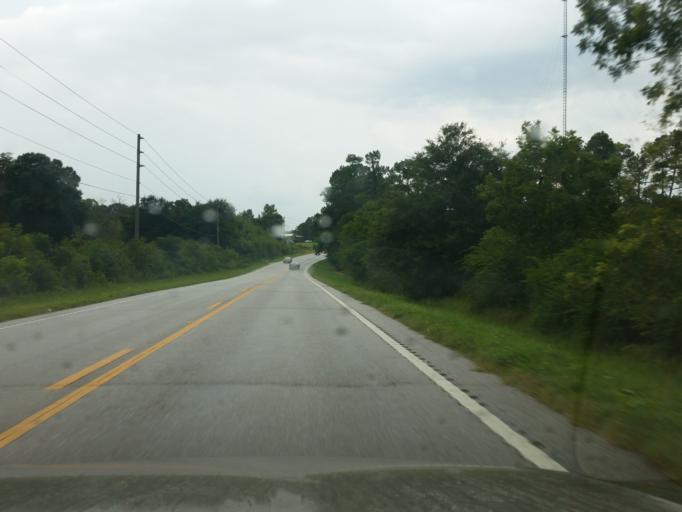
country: US
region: Alabama
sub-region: Baldwin County
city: Elberta
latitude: 30.5450
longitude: -87.5759
